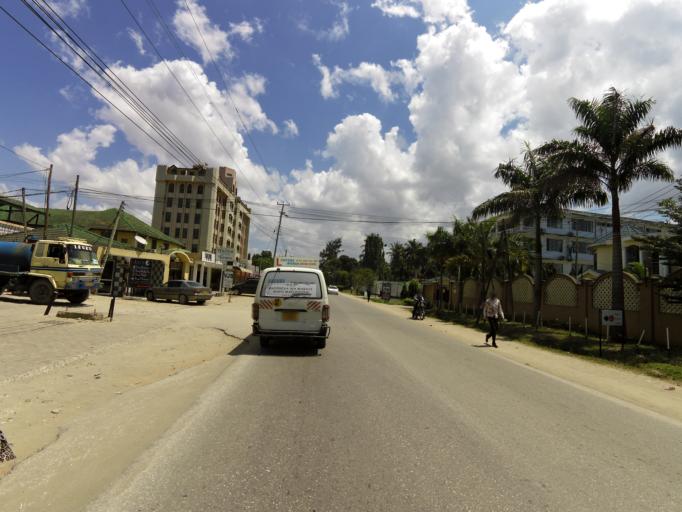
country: TZ
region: Dar es Salaam
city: Magomeni
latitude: -6.7616
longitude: 39.2513
